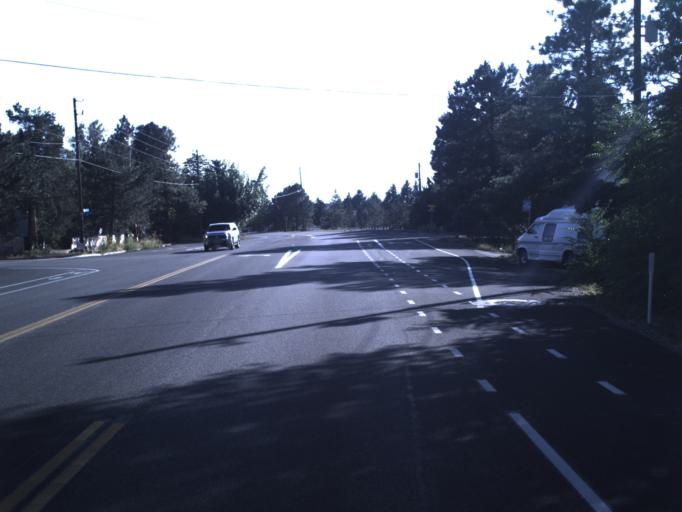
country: US
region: Utah
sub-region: Salt Lake County
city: Cottonwood Heights
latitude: 40.6001
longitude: -111.7972
